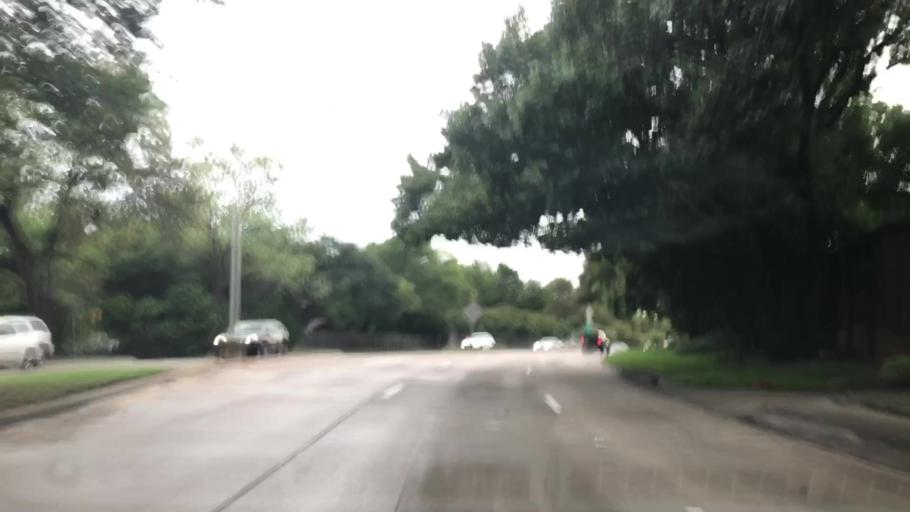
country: US
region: Texas
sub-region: Dallas County
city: University Park
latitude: 32.8968
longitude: -96.7749
